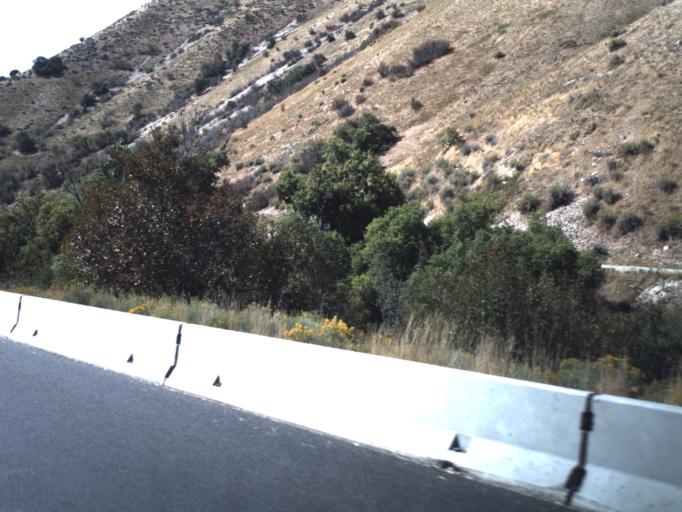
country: US
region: Utah
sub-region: Box Elder County
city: Brigham City
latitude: 41.4986
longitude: -111.9518
